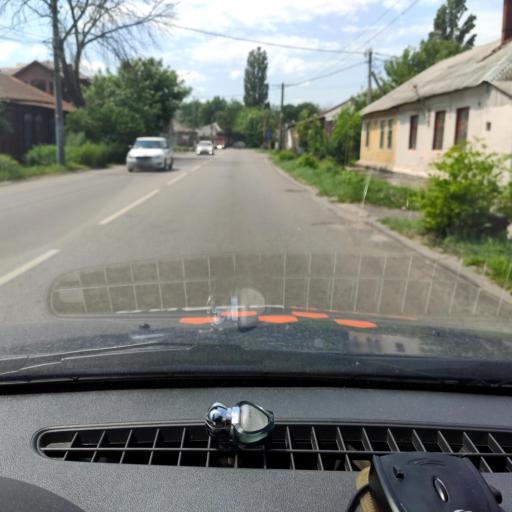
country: RU
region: Voronezj
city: Voronezh
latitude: 51.6825
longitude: 39.2056
